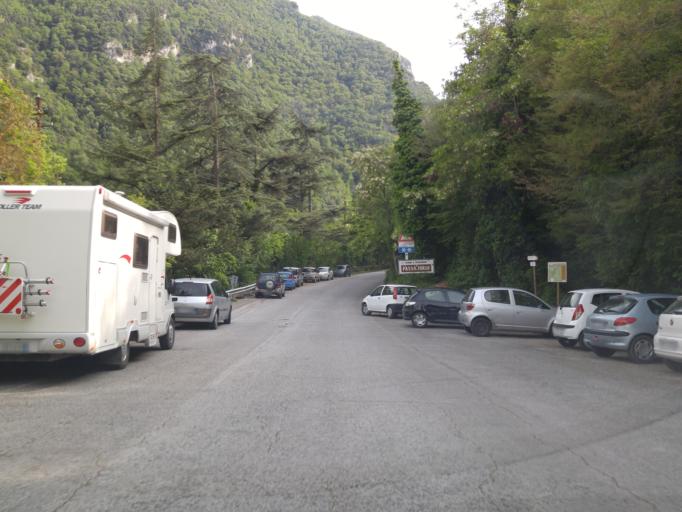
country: IT
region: The Marches
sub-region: Provincia di Pesaro e Urbino
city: Canavaccio
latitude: 43.6579
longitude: 12.7342
